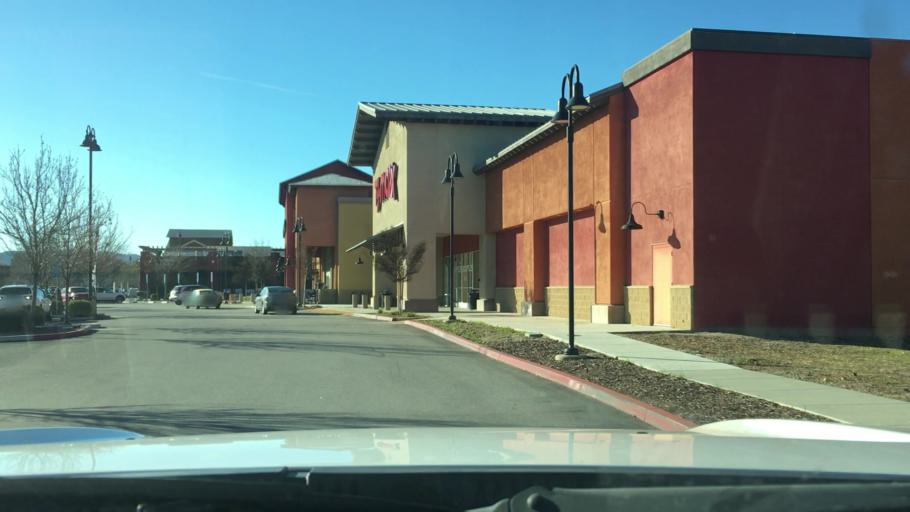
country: US
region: California
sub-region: San Luis Obispo County
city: Paso Robles
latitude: 35.6463
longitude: -120.6592
